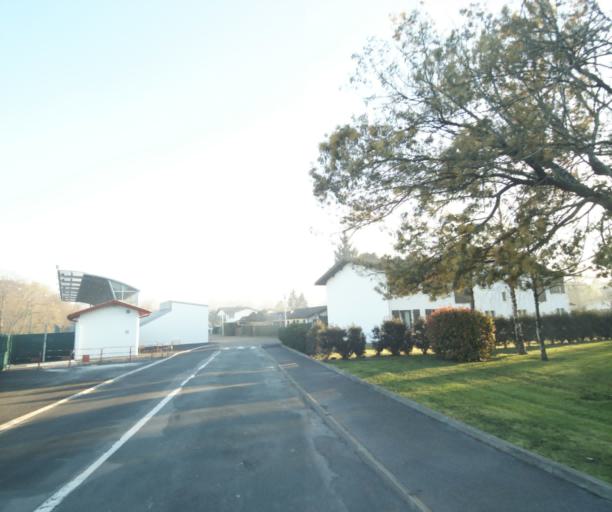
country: FR
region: Aquitaine
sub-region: Departement des Pyrenees-Atlantiques
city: Urrugne
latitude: 43.3655
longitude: -1.6943
